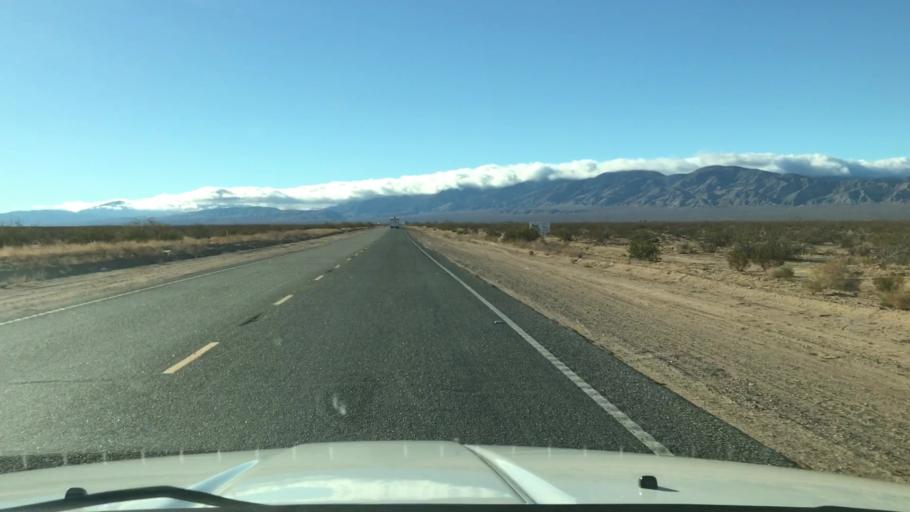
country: US
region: California
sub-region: Kern County
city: California City
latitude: 35.1255
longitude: -118.0457
